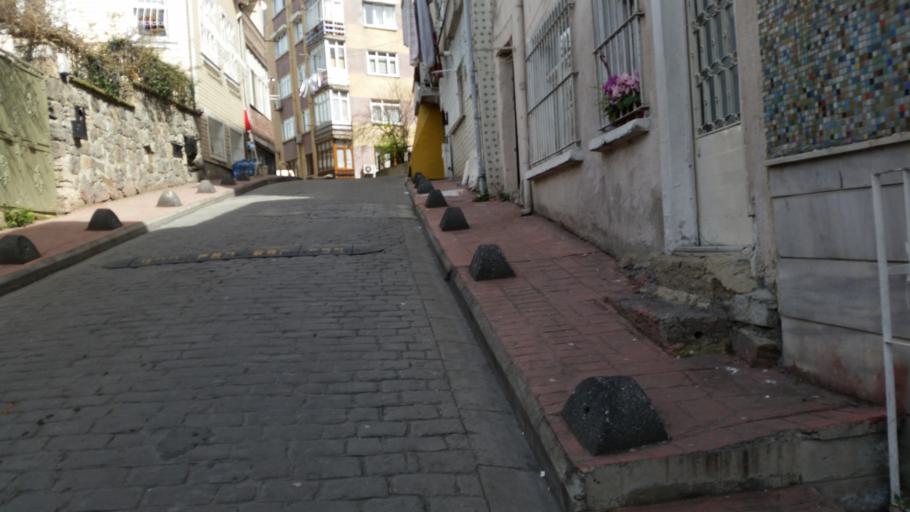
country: TR
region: Istanbul
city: Eminoenue
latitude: 41.0344
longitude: 28.9708
